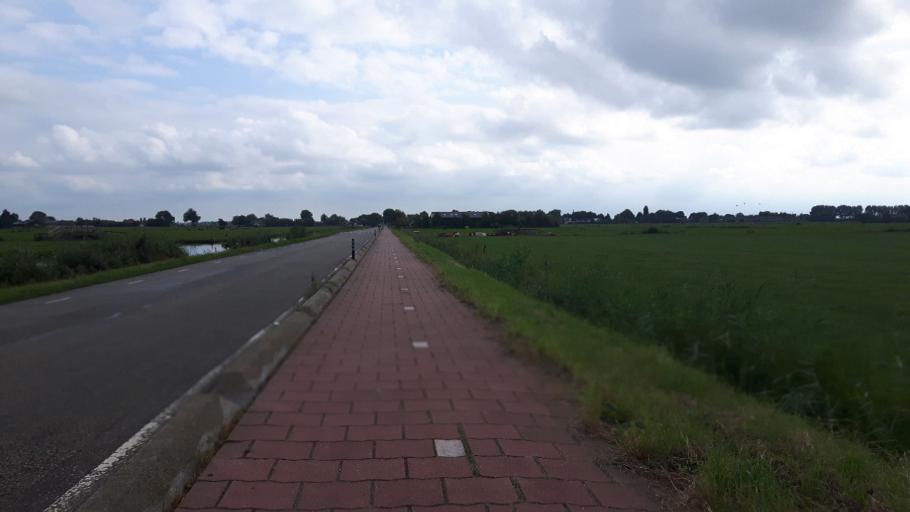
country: NL
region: Utrecht
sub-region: Gemeente De Ronde Venen
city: Mijdrecht
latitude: 52.2309
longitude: 4.9039
